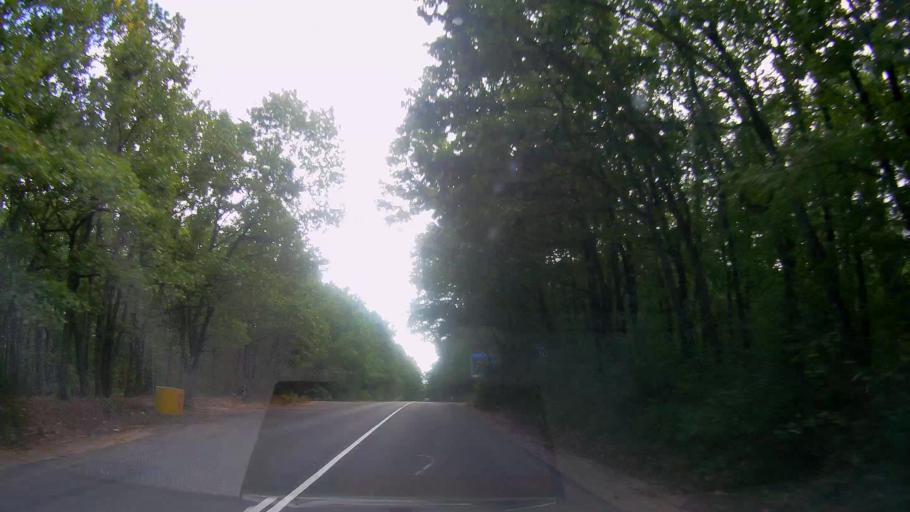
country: BG
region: Burgas
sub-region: Obshtina Primorsko
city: Primorsko
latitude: 42.2840
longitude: 27.7371
